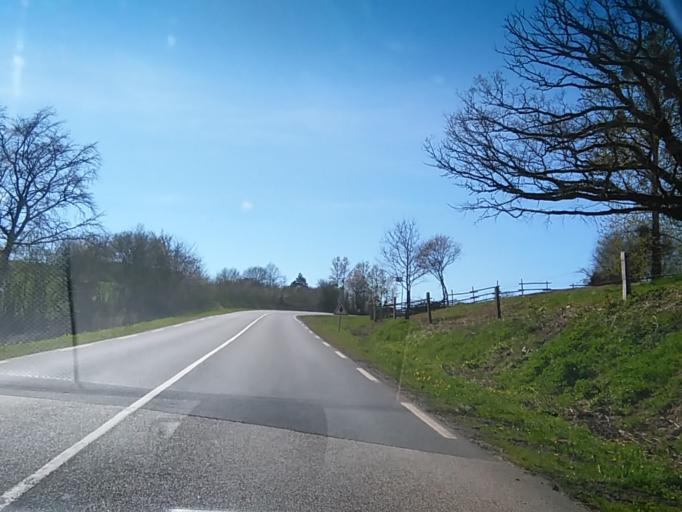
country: FR
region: Lower Normandy
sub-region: Departement de l'Orne
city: Saint-Denis-sur-Sarthon
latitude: 48.5127
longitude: -0.0300
